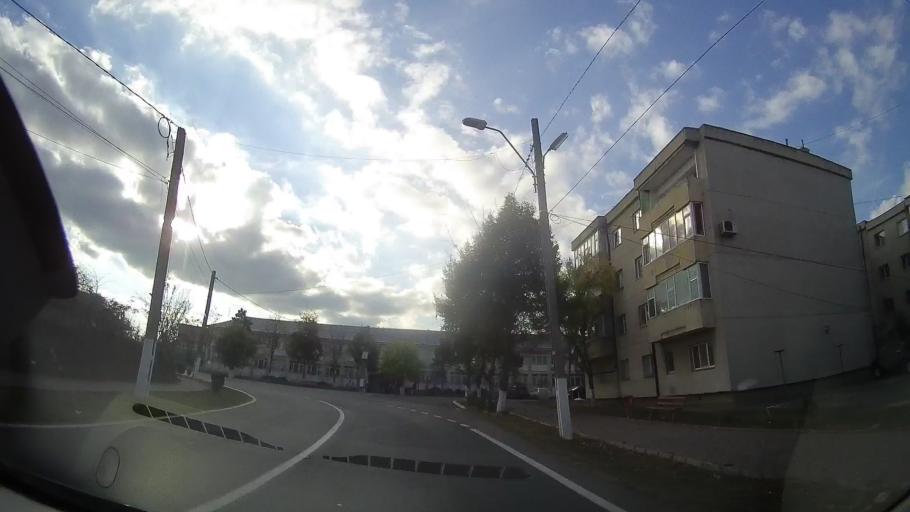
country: RO
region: Constanta
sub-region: Comuna Negru Voda
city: Negru Voda
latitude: 43.8175
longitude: 28.2095
